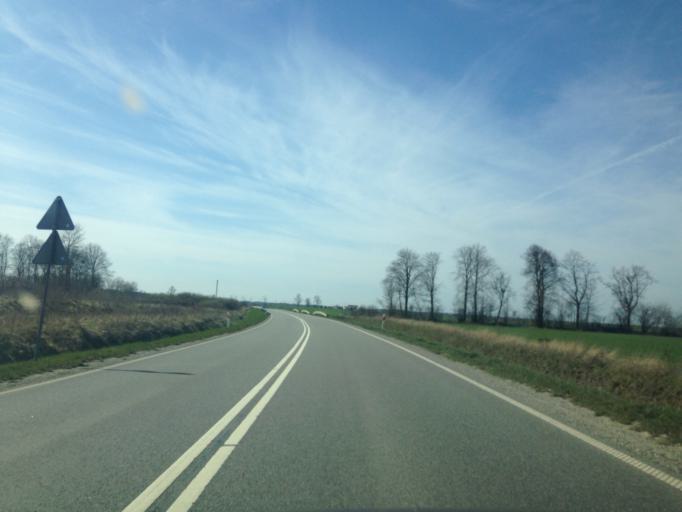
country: PL
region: Pomeranian Voivodeship
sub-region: Powiat starogardzki
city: Smetowo Graniczne
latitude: 53.7423
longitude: 18.6640
